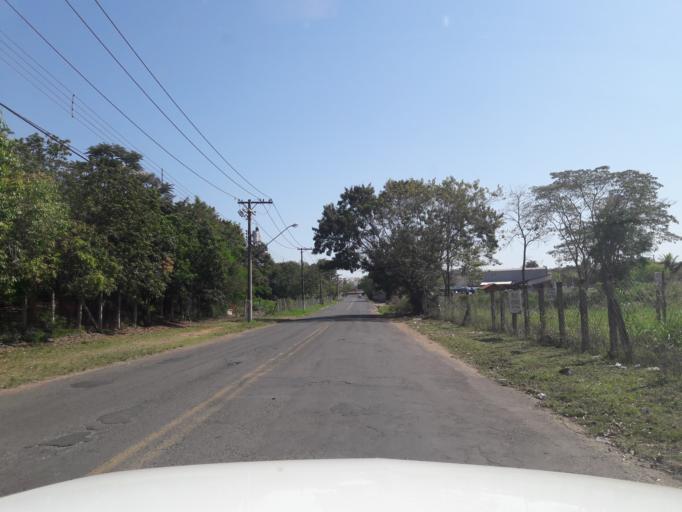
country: BR
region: Sao Paulo
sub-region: Moji-Guacu
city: Mogi-Gaucu
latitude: -22.3663
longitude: -46.9520
